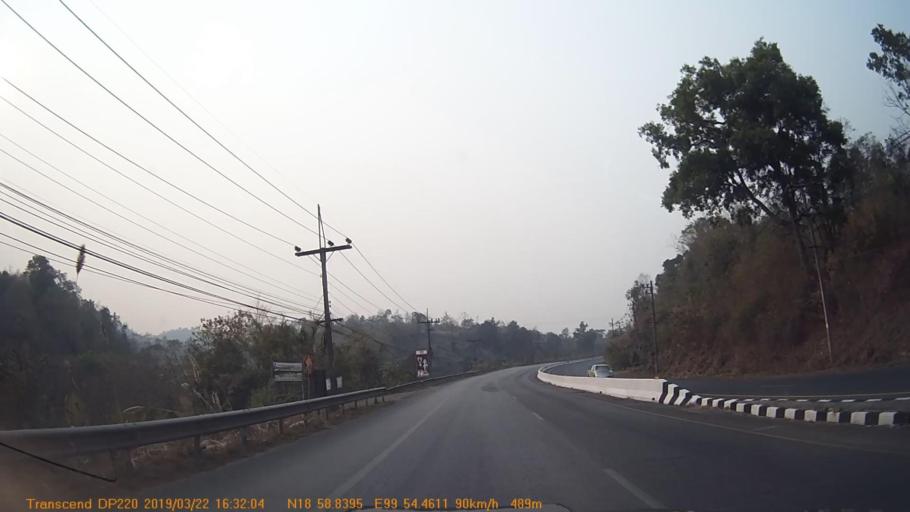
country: TH
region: Phayao
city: Dok Kham Tai
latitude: 18.9810
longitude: 99.9074
